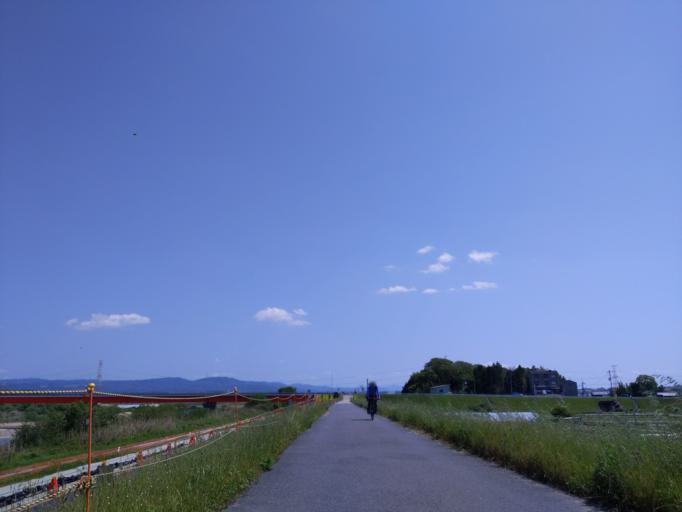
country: JP
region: Kyoto
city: Tanabe
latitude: 34.7709
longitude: 135.8011
